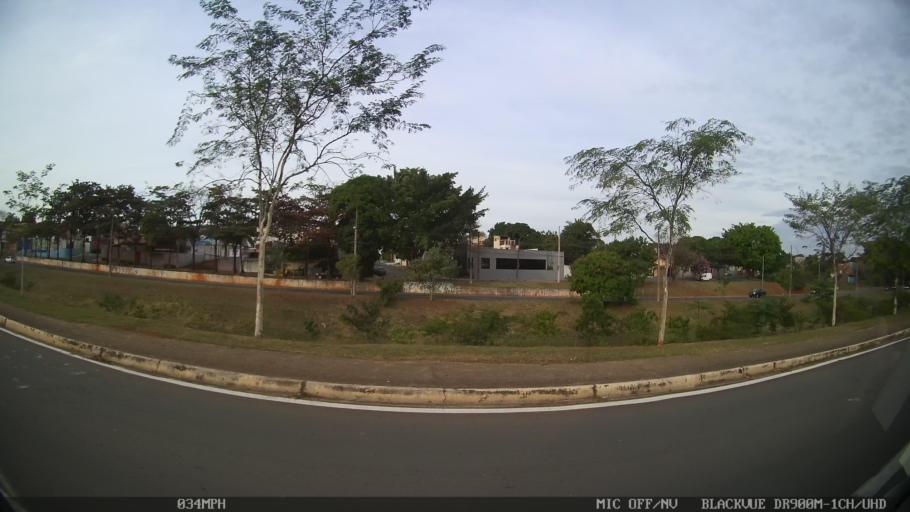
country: BR
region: Sao Paulo
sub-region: Limeira
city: Limeira
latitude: -22.5681
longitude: -47.4160
